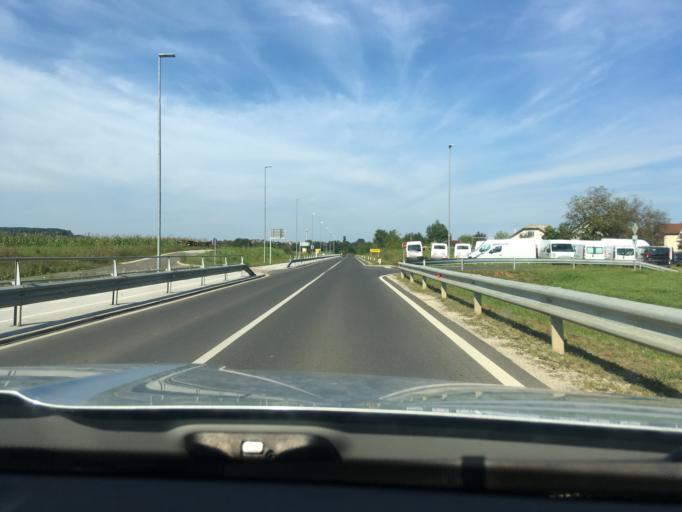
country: SI
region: Crnomelj
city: Crnomelj
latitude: 45.5655
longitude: 15.1744
